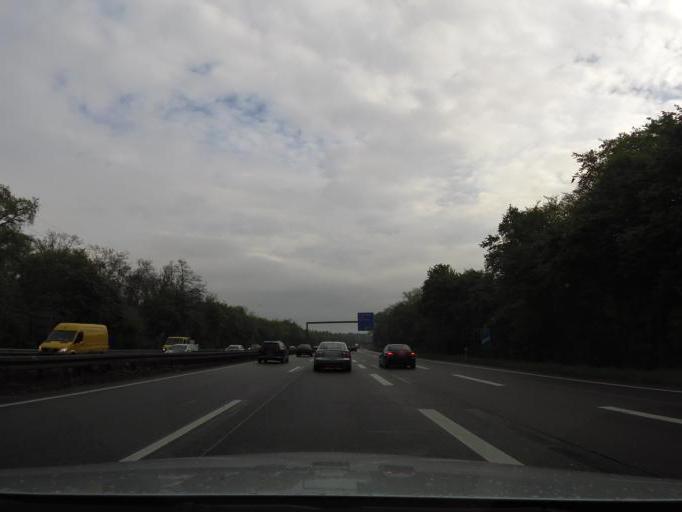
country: DE
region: Hesse
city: Raunheim
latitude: 49.9849
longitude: 8.4659
